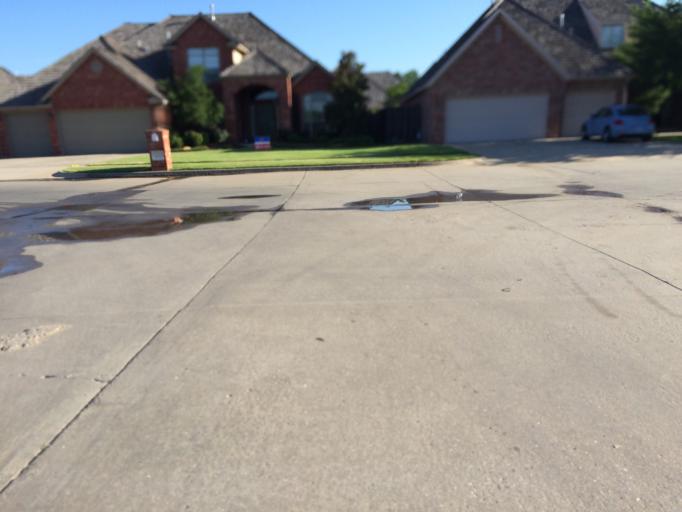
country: US
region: Oklahoma
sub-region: Cleveland County
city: Norman
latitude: 35.2314
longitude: -97.5004
